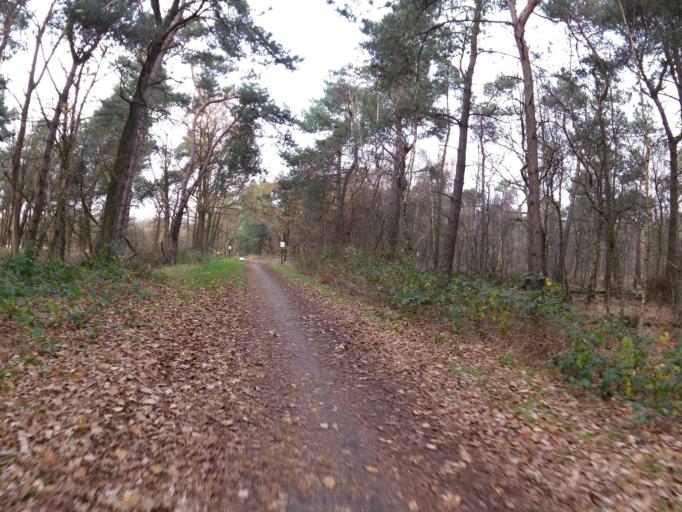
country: NL
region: North Brabant
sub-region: Gemeente Oss
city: Berghem
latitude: 51.7256
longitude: 5.5775
